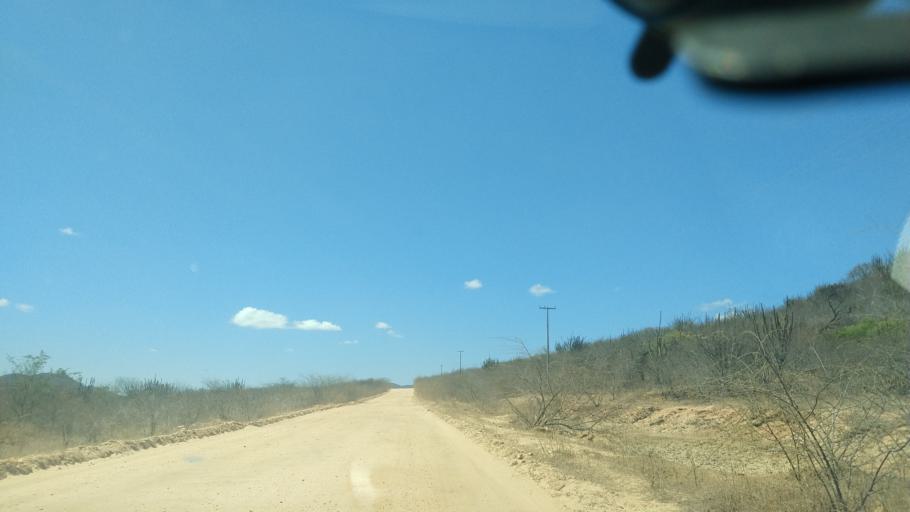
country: BR
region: Rio Grande do Norte
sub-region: Sao Tome
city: Sao Tome
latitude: -5.9709
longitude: -36.1628
